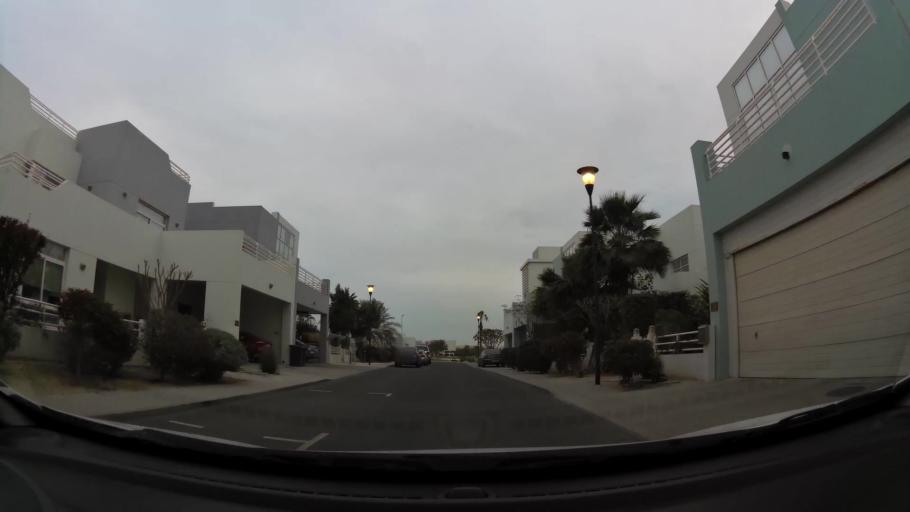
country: BH
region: Northern
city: Ar Rifa'
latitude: 26.0998
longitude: 50.5635
